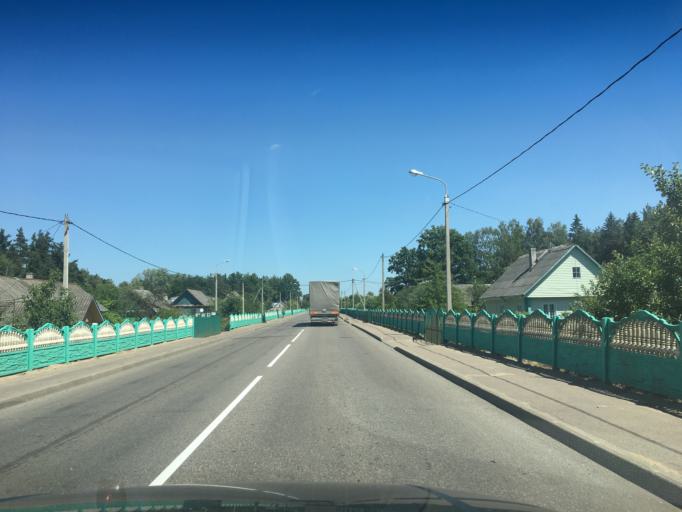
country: BY
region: Grodnenskaya
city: Iwye
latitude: 54.0265
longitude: 25.9212
